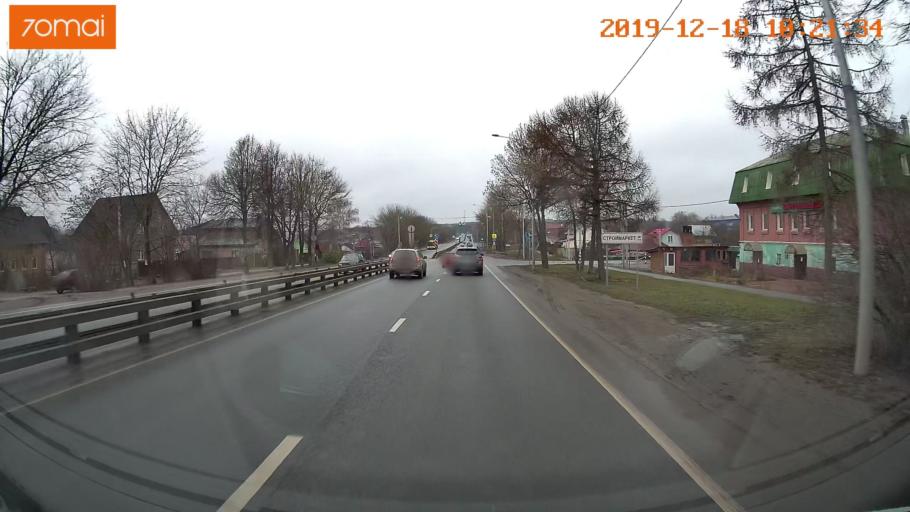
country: RU
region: Moskovskaya
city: Dubrovitsy
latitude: 55.3866
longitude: 37.4171
